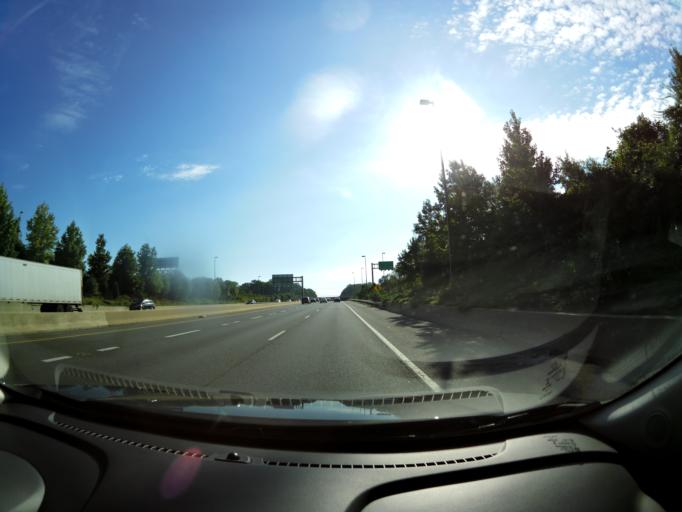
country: US
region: Maryland
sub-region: Montgomery County
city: North Bethesda
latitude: 39.0315
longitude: -77.1316
